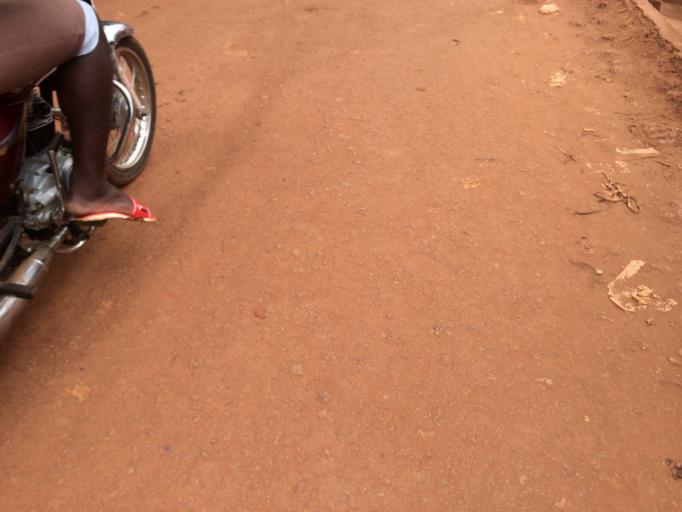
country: UG
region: Central Region
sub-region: Kampala District
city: Kampala
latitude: 0.2916
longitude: 32.6037
